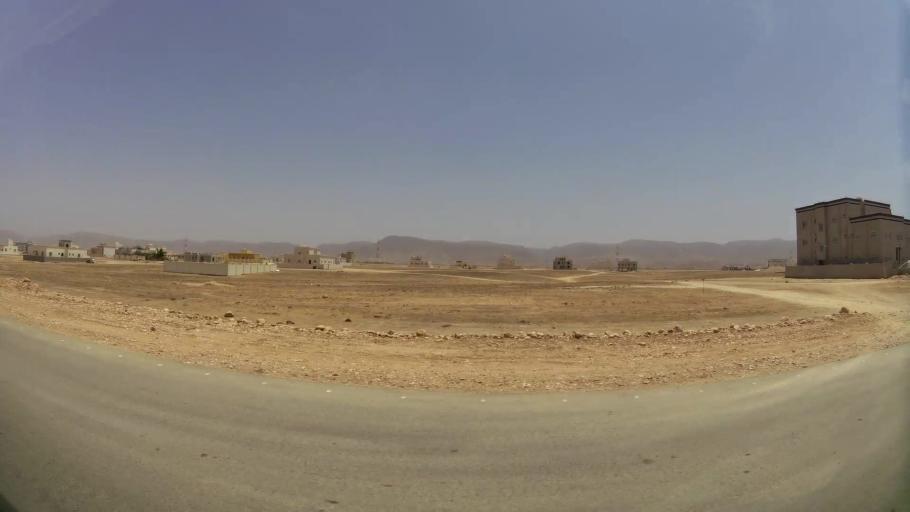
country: OM
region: Zufar
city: Salalah
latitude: 17.0979
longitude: 54.1978
